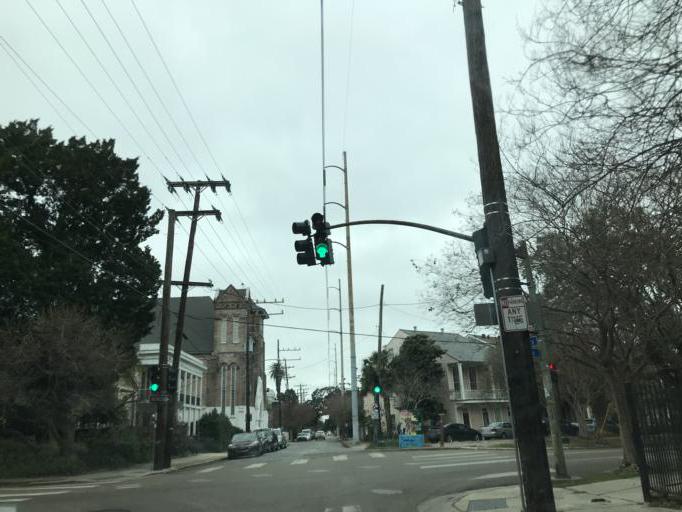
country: US
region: Louisiana
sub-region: Orleans Parish
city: New Orleans
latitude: 29.9330
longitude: -90.0740
